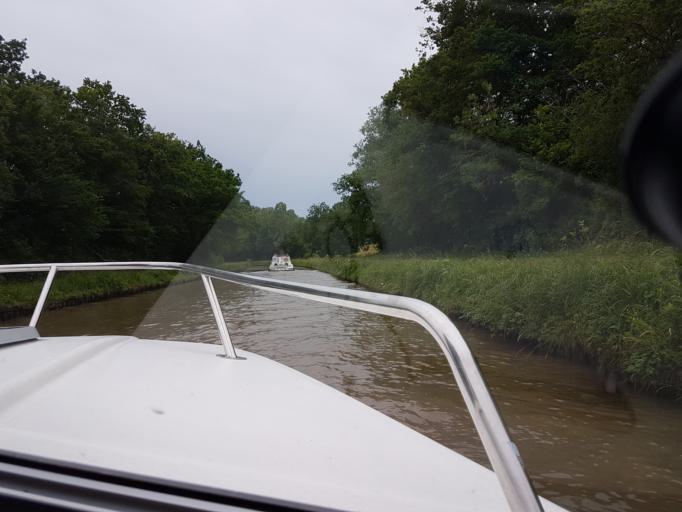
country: FR
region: Bourgogne
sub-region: Departement de la Nievre
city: Clamecy
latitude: 47.3916
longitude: 3.5994
